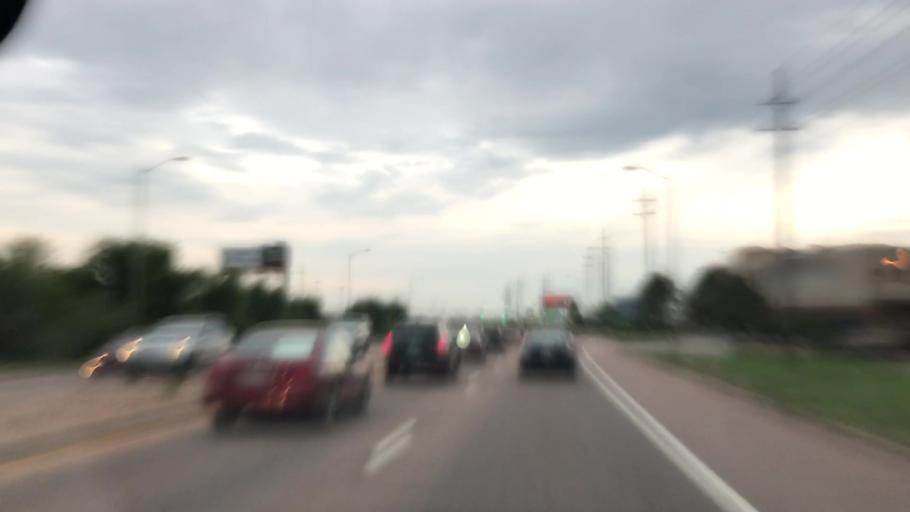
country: US
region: Colorado
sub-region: El Paso County
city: Colorado Springs
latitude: 38.8324
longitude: -104.8431
